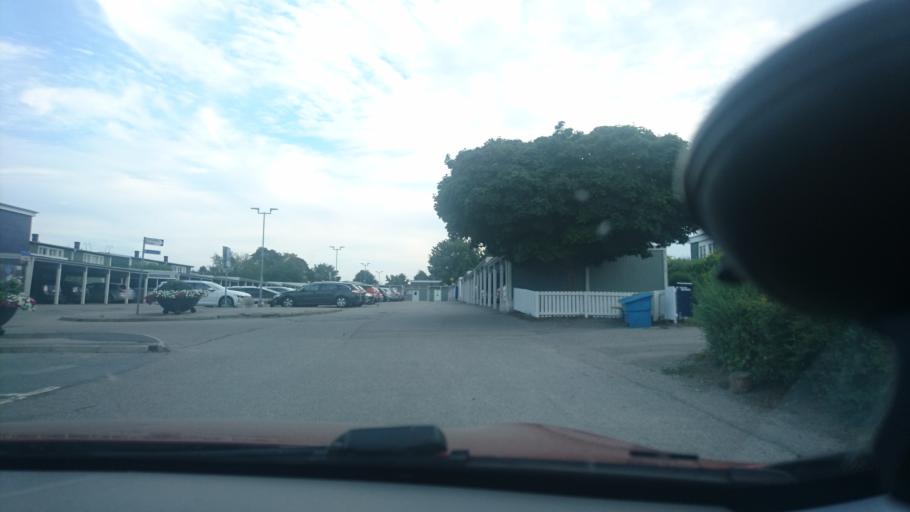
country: SE
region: Stockholm
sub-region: Upplands Vasby Kommun
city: Upplands Vaesby
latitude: 59.5086
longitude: 17.9153
